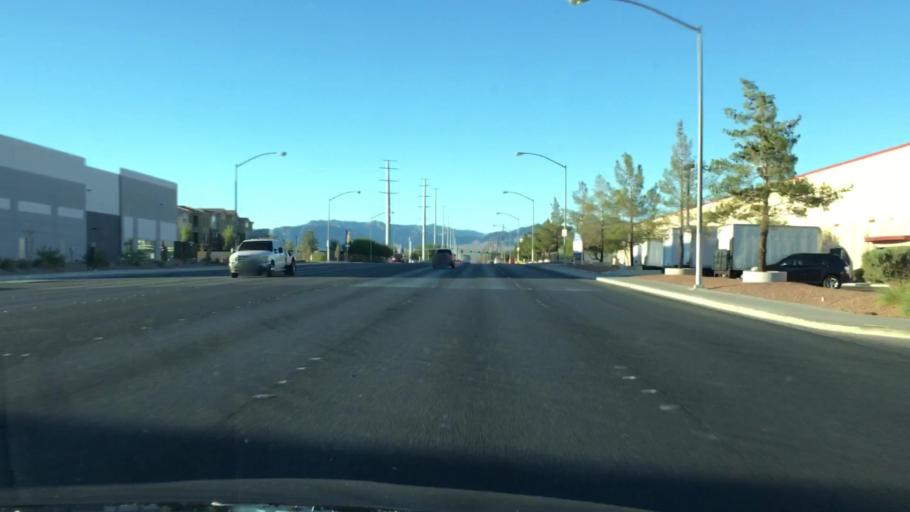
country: US
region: Nevada
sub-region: Clark County
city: Nellis Air Force Base
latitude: 36.2374
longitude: -115.0800
